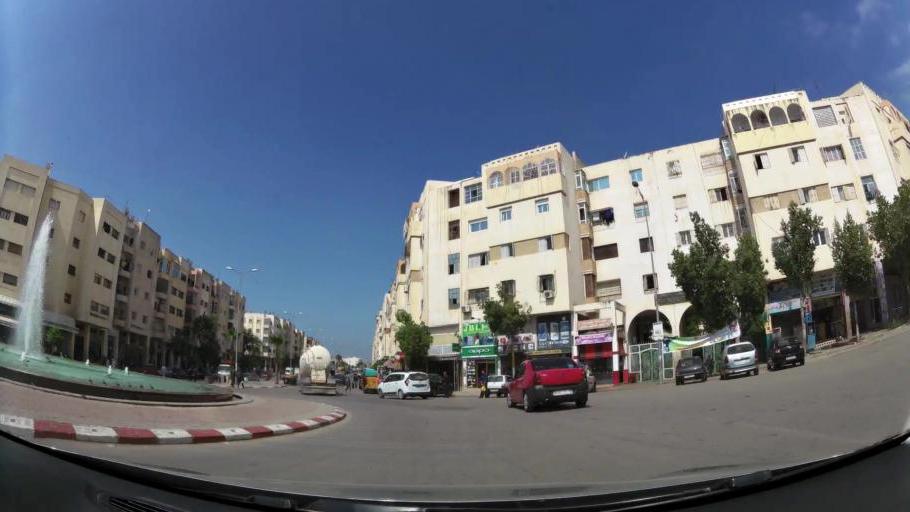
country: MA
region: Fes-Boulemane
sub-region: Fes
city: Fes
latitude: 34.0578
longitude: -5.0305
